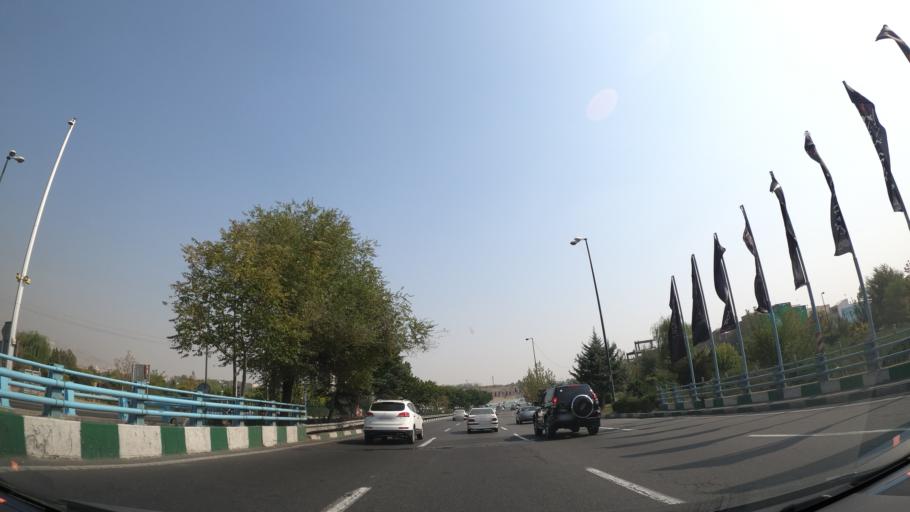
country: IR
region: Tehran
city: Shahr-e Qods
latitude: 35.7571
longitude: 51.2658
